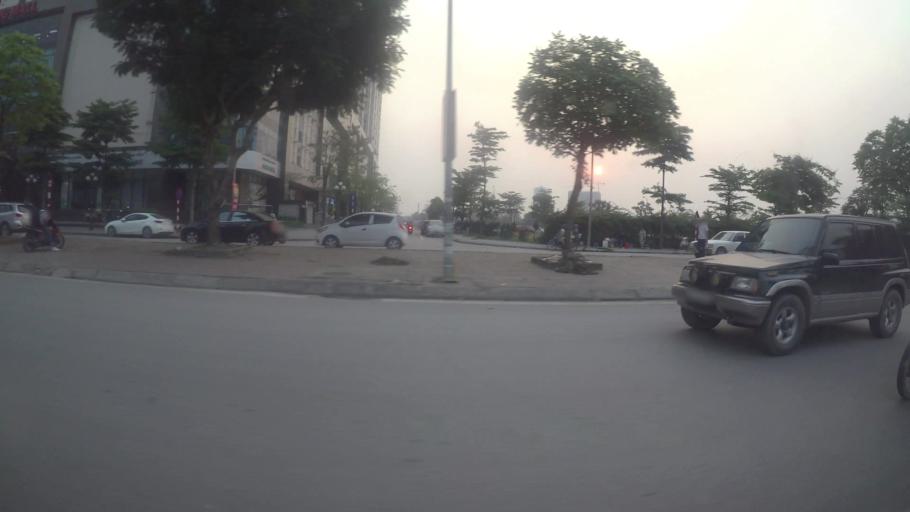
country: VN
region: Ha Noi
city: Cau Dien
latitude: 21.0089
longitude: 105.7309
